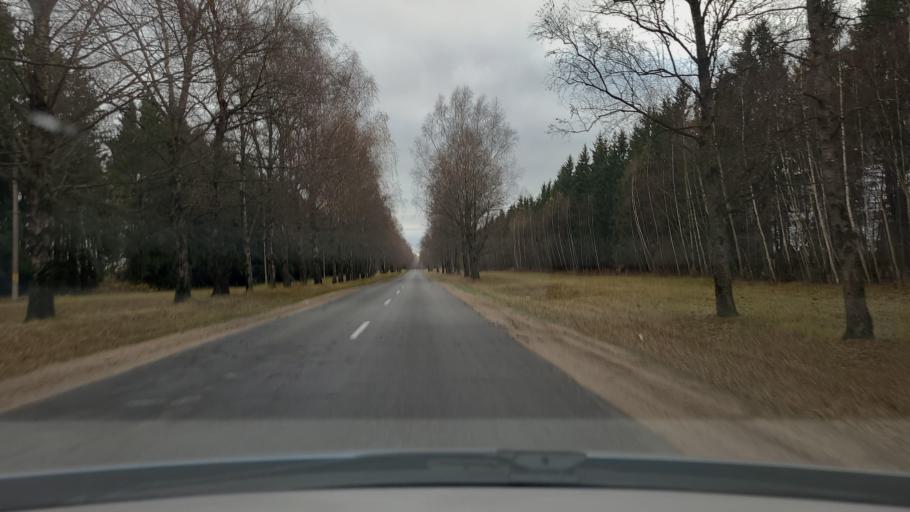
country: BY
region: Minsk
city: Khalopyenichy
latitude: 54.4915
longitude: 28.9546
